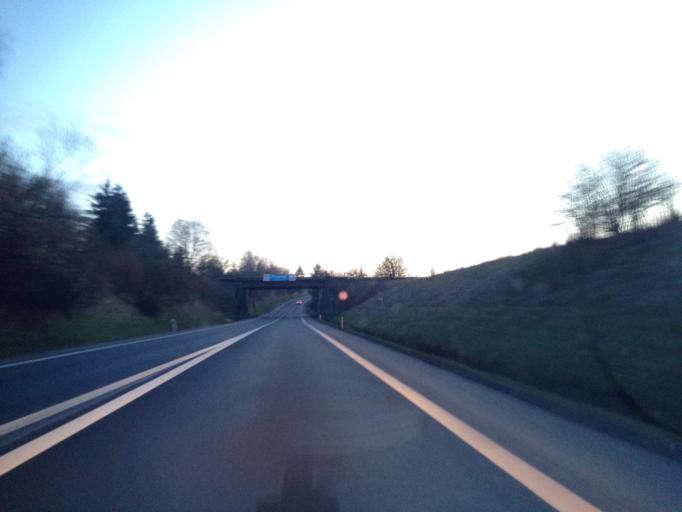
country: CZ
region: Ustecky
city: Kryry
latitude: 50.1382
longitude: 13.4350
